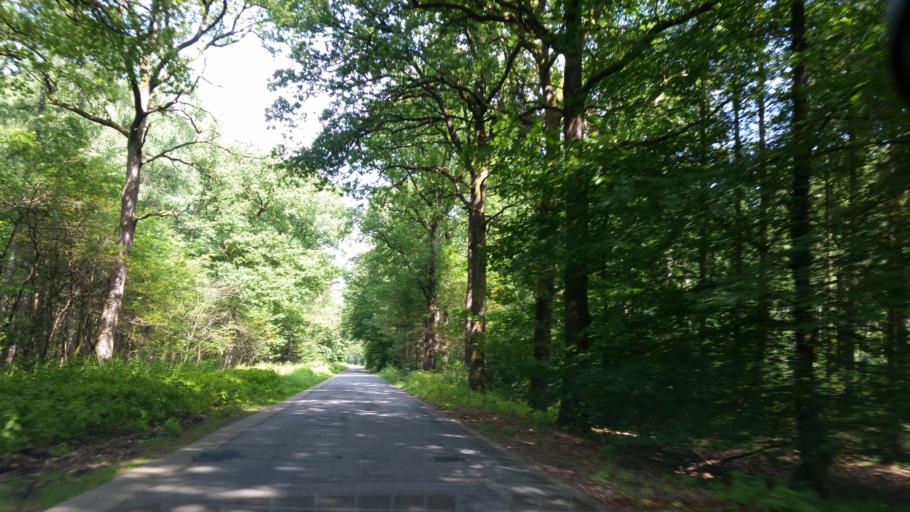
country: DE
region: Lower Saxony
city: Bispingen
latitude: 53.0952
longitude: 9.9072
